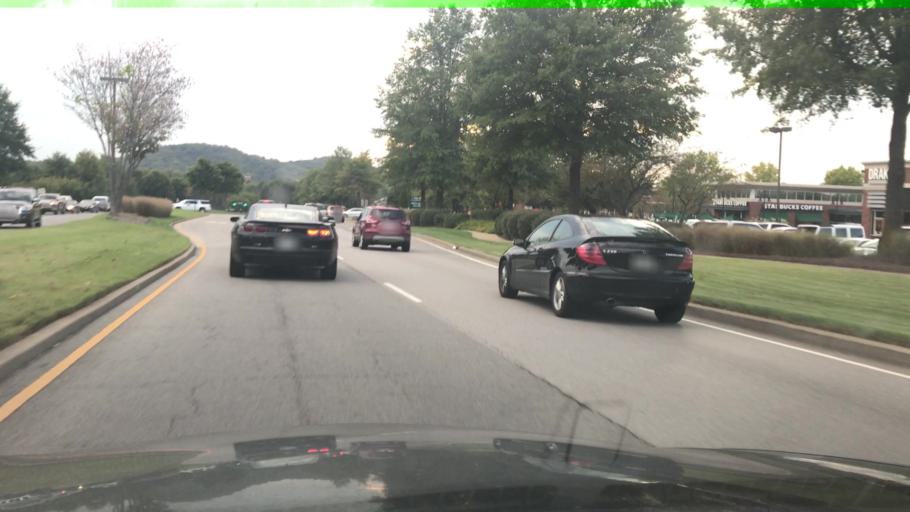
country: US
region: Tennessee
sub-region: Williamson County
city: Franklin
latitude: 35.9475
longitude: -86.8206
